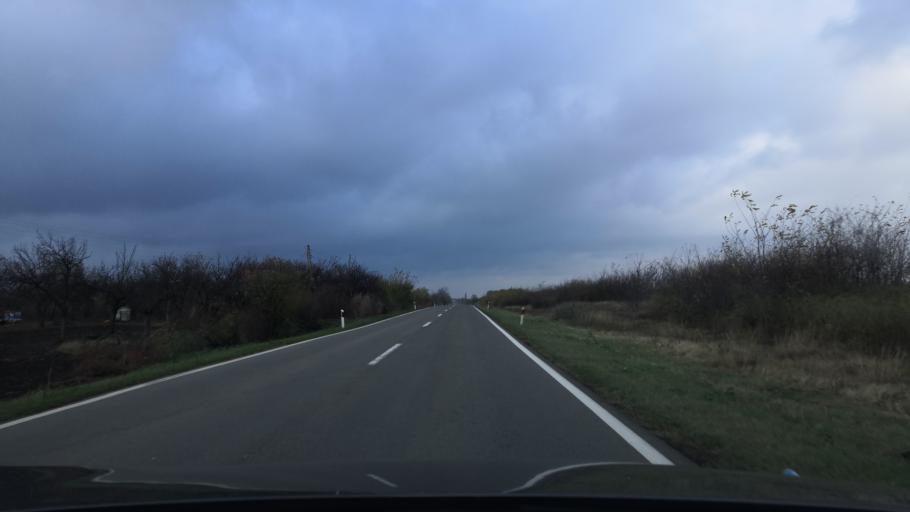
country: RS
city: Sanad
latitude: 45.9681
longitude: 20.1247
